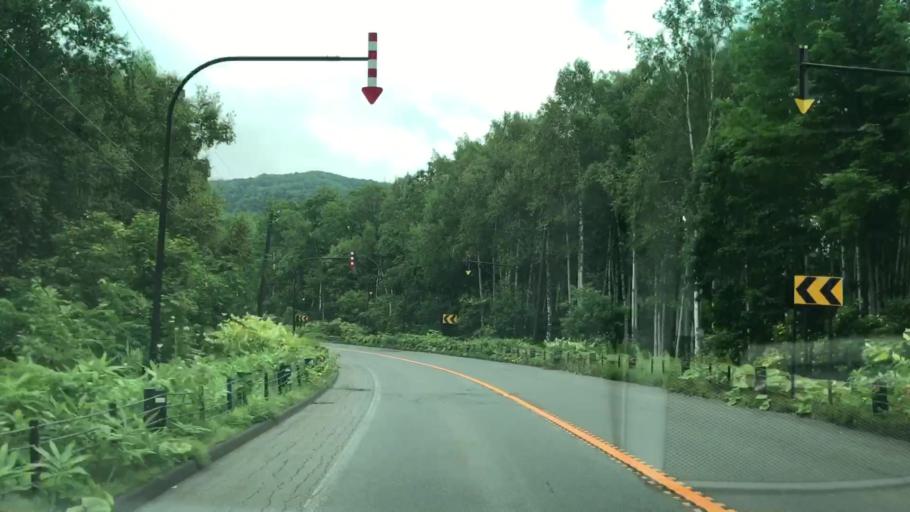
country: JP
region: Hokkaido
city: Otaru
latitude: 43.0070
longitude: 140.8763
